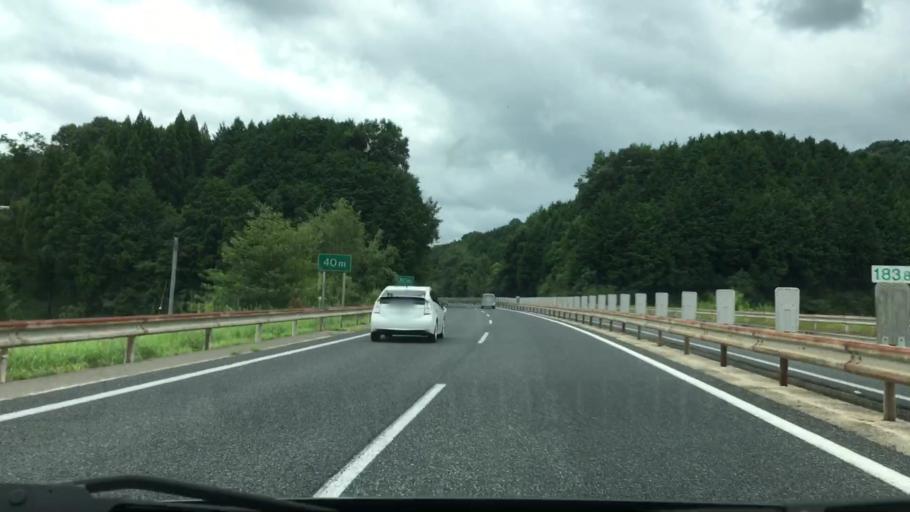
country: JP
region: Okayama
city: Takahashi
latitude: 35.0155
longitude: 133.7300
